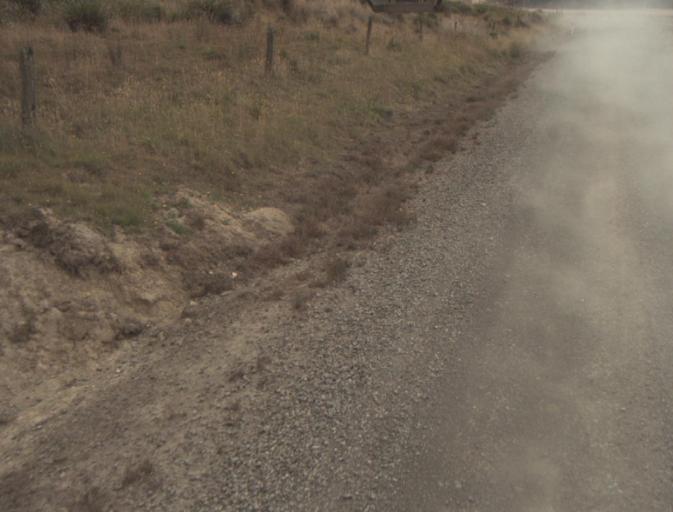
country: AU
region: Tasmania
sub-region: Northern Midlands
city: Evandale
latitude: -41.4802
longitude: 147.4430
